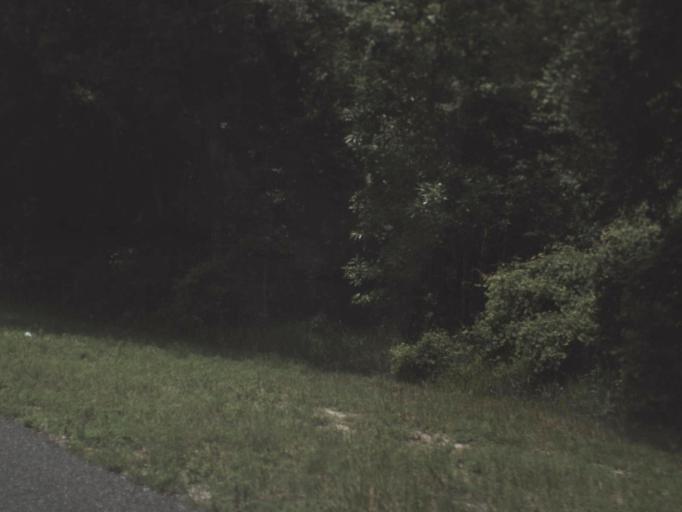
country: US
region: Florida
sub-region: Taylor County
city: Perry
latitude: 29.9321
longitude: -83.4449
